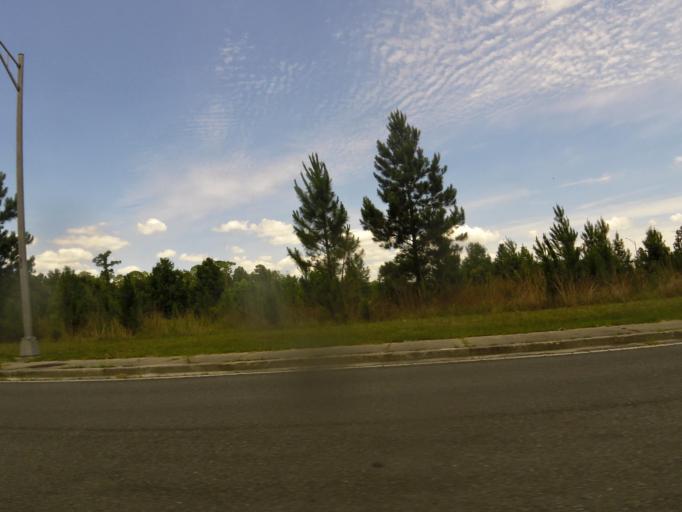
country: US
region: Florida
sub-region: Duval County
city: Jacksonville
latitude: 30.4728
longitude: -81.6082
